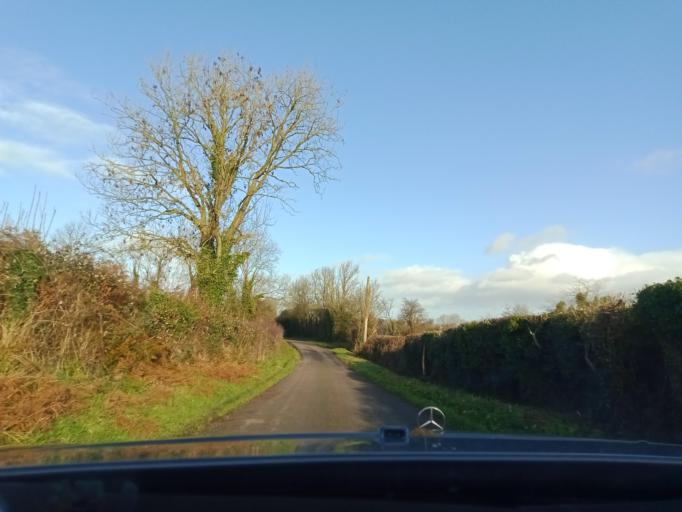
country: IE
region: Leinster
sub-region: Kilkenny
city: Callan
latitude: 52.4996
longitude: -7.3548
